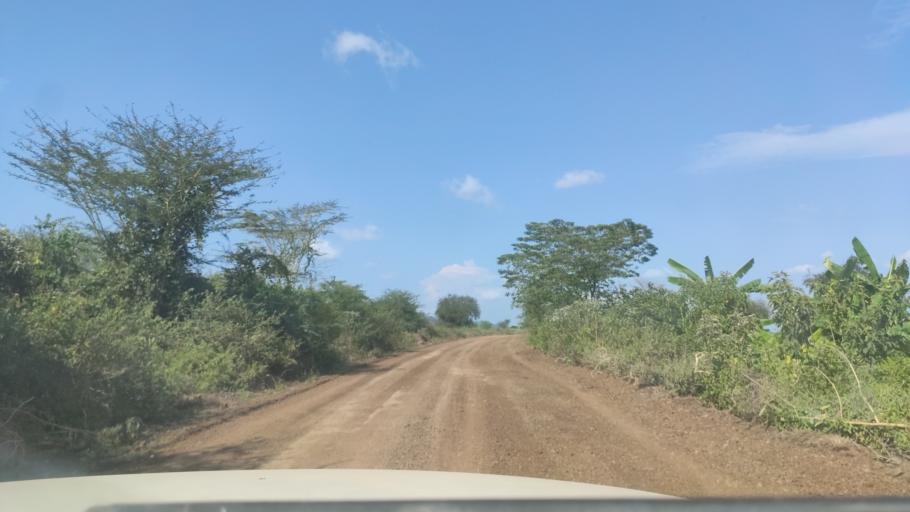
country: ET
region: Southern Nations, Nationalities, and People's Region
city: Felege Neway
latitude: 6.3776
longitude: 37.0885
